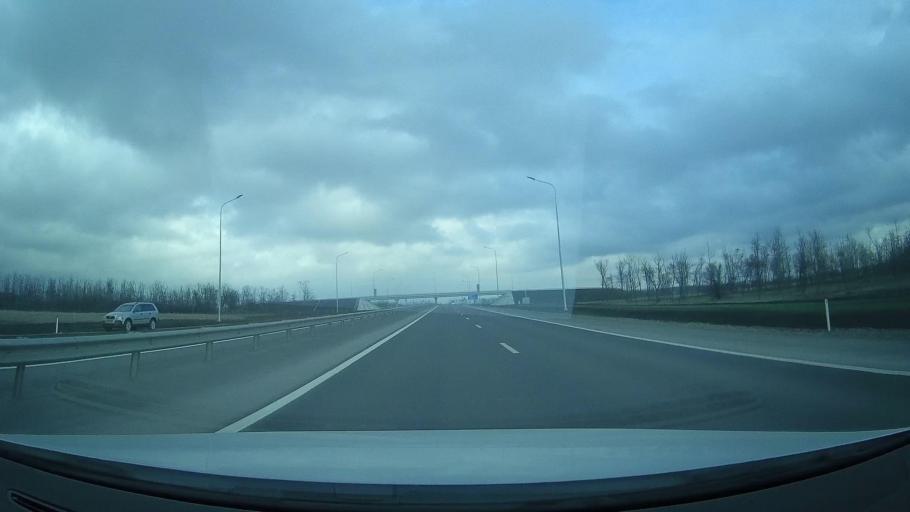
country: RU
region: Rostov
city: Grushevskaya
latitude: 47.4919
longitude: 39.9473
